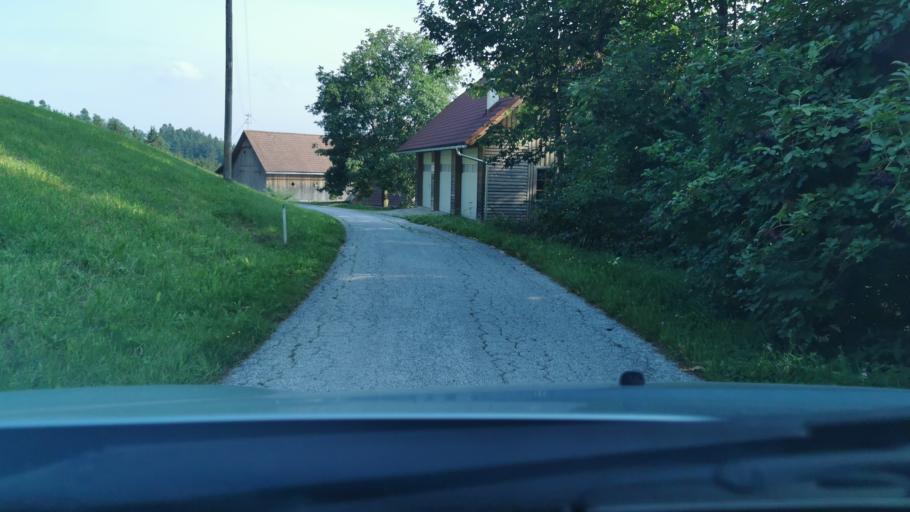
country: AT
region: Styria
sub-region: Politischer Bezirk Weiz
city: Fischbach
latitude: 47.3890
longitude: 15.6319
